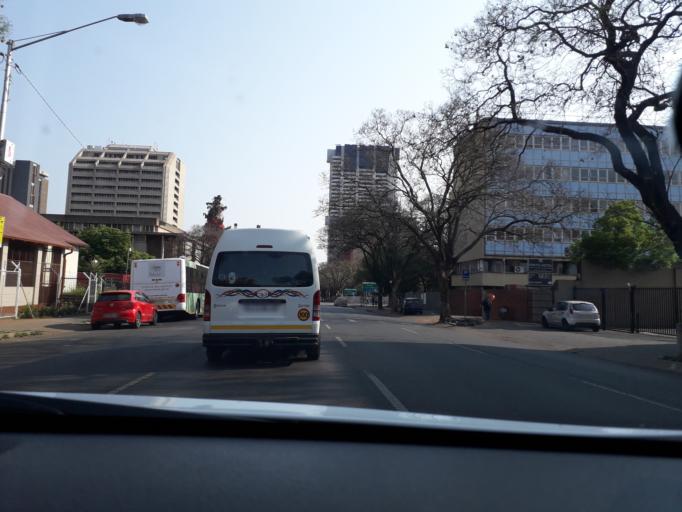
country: ZA
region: Gauteng
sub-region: City of Tshwane Metropolitan Municipality
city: Pretoria
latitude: -25.7516
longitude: 28.1934
